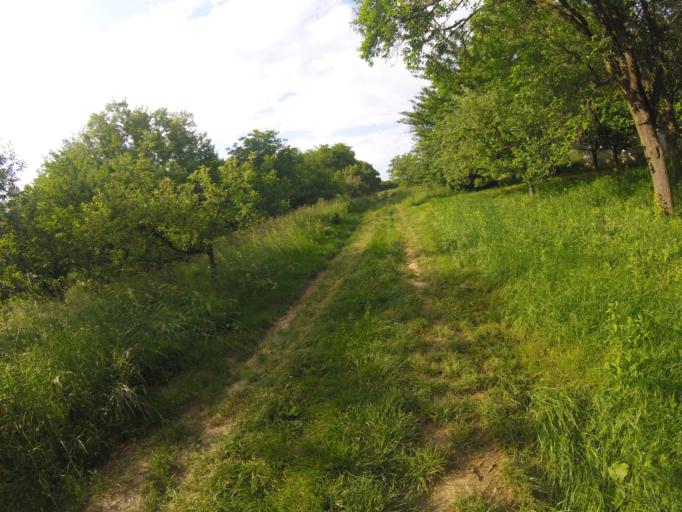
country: HU
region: Zala
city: Zalaszentgrot
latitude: 46.8794
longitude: 17.1250
